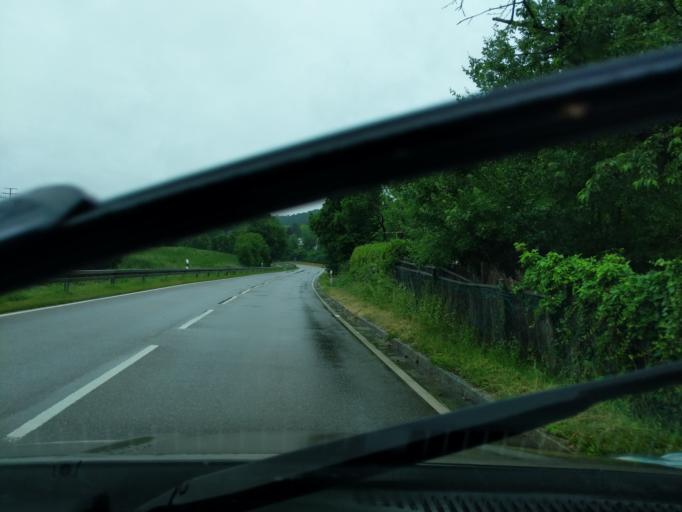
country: DE
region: Bavaria
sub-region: Upper Palatinate
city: Sinzing
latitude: 49.0326
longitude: 12.0324
